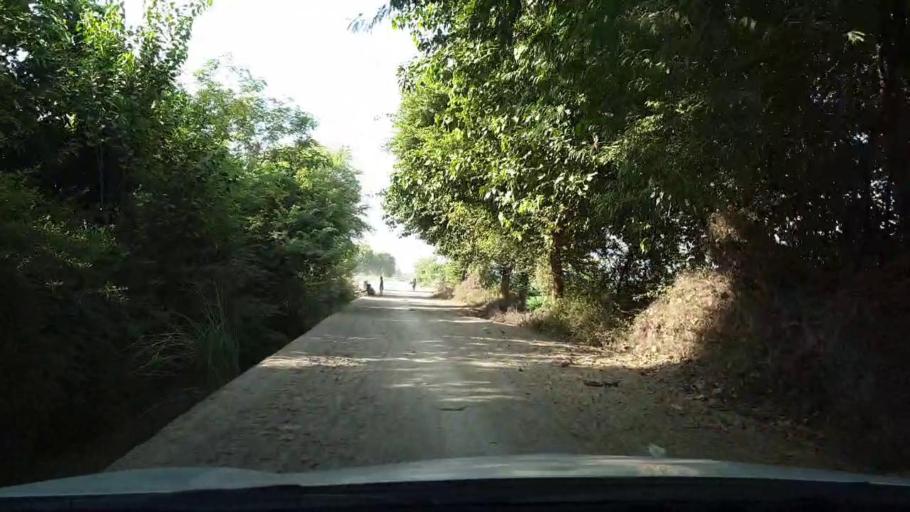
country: PK
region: Sindh
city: Larkana
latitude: 27.5464
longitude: 68.2674
